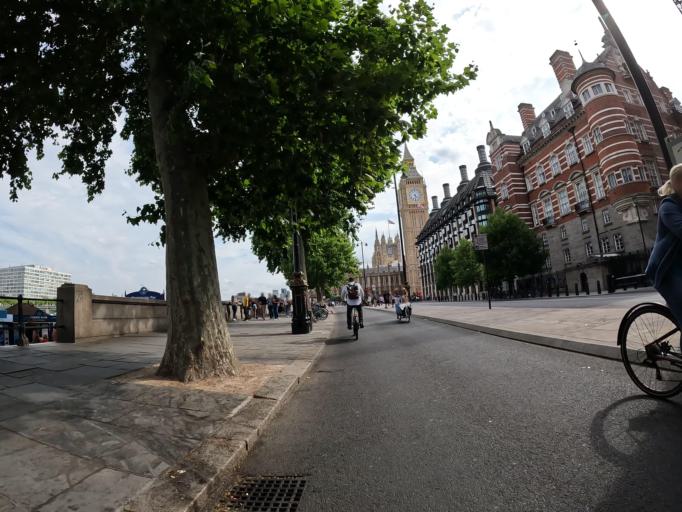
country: GB
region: England
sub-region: Greater London
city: Orpington
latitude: 51.3660
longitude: 0.0516
